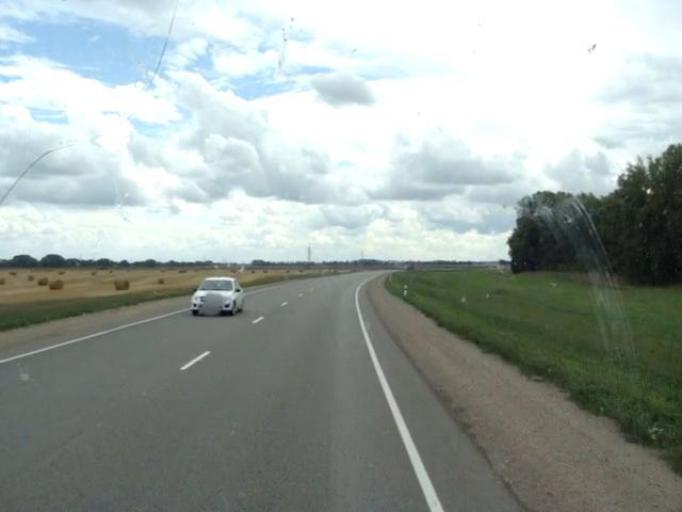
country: RU
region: Altai Krai
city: Shubenka
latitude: 52.6822
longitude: 85.0465
